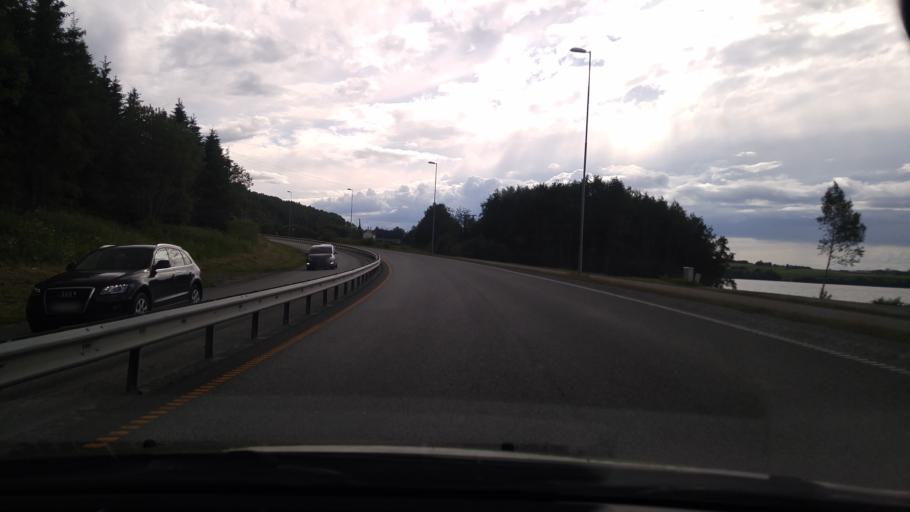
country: NO
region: Nord-Trondelag
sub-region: Levanger
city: Levanger
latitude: 63.7307
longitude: 11.2795
